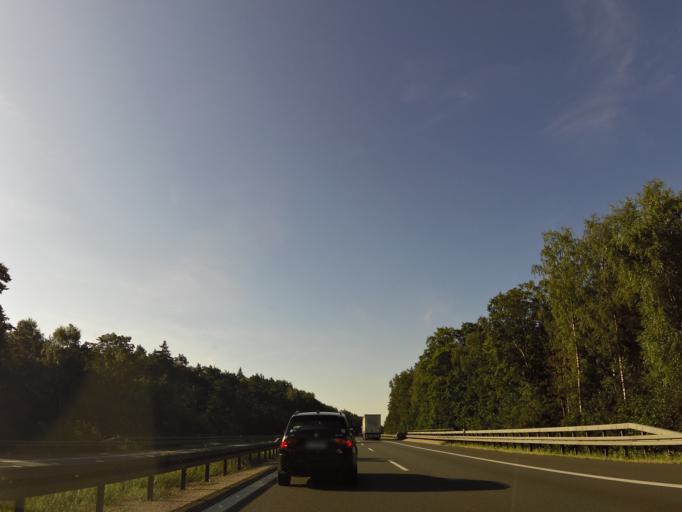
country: DE
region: Bavaria
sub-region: Regierungsbezirk Mittelfranken
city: Hessdorf
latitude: 49.6143
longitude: 10.9247
